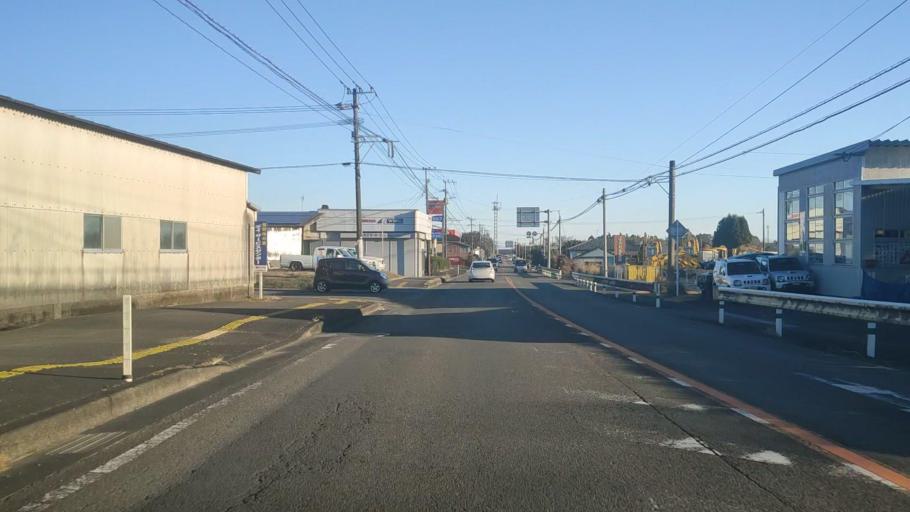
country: JP
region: Miyazaki
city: Takanabe
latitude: 32.1741
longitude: 131.5196
